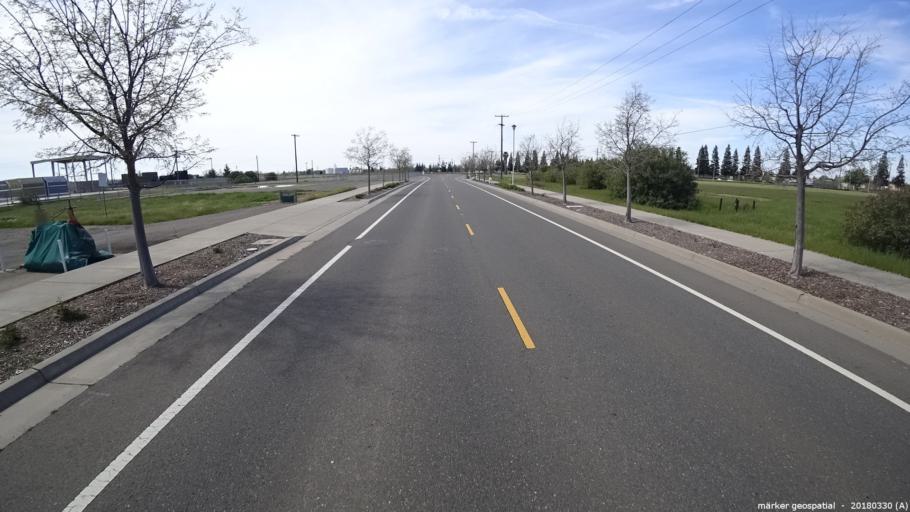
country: US
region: California
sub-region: Sacramento County
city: Rancho Cordova
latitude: 38.5641
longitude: -121.3068
